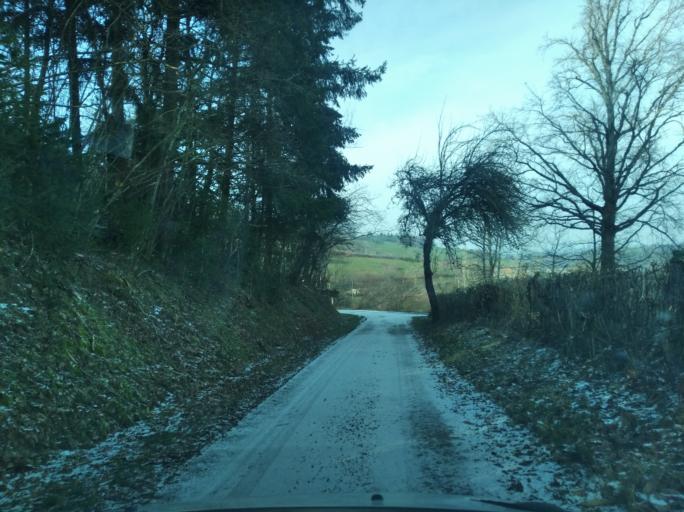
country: FR
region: Rhone-Alpes
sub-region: Departement de la Loire
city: La Pacaudiere
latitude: 46.1548
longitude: 3.7557
